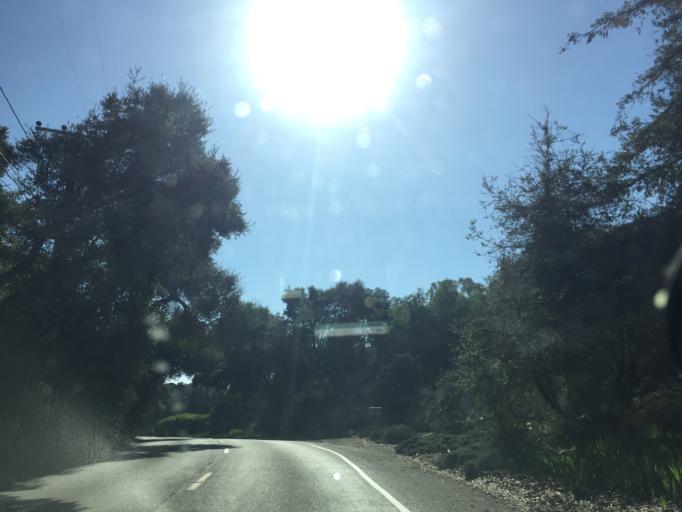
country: US
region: California
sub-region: Santa Barbara County
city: Goleta
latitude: 34.4306
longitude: -119.7700
